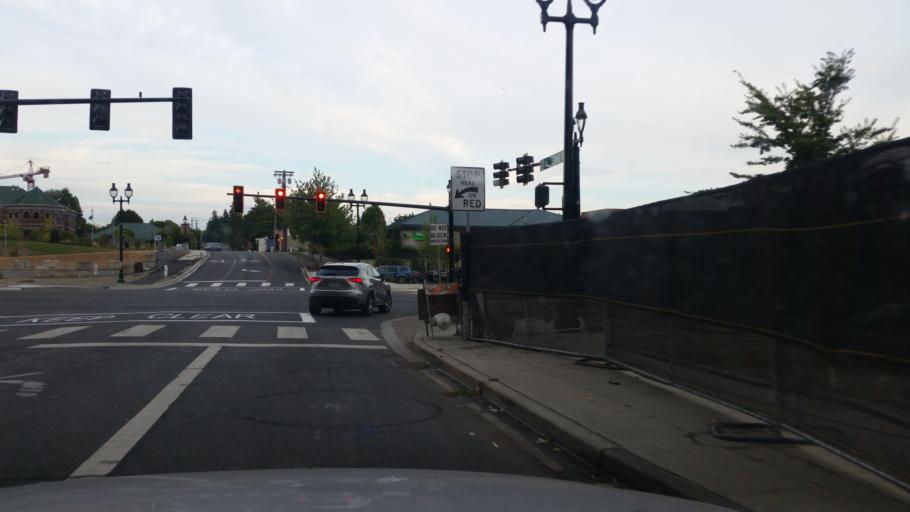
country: US
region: Washington
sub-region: King County
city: Bothell
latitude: 47.7608
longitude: -122.2081
